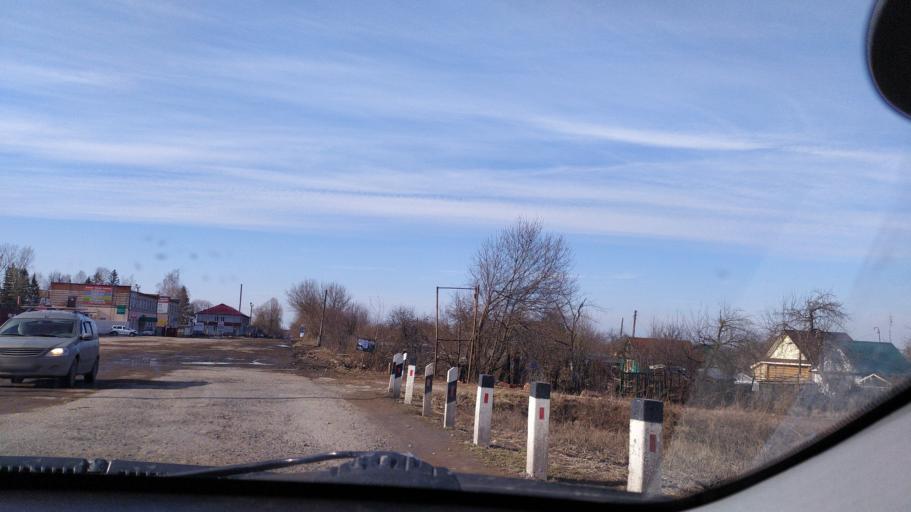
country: RU
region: Chuvashia
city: Novyye Lapsary
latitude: 56.0774
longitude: 47.2248
